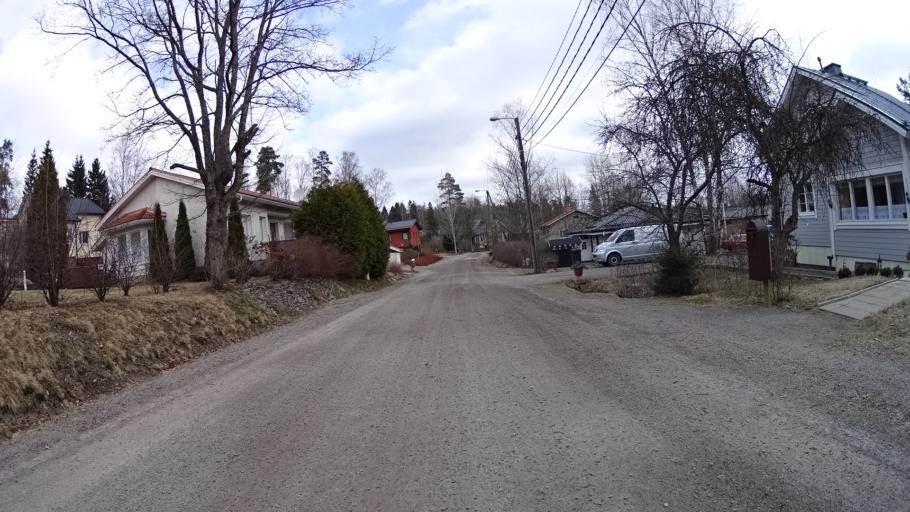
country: FI
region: Uusimaa
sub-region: Helsinki
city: Kilo
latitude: 60.2414
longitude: 24.7715
